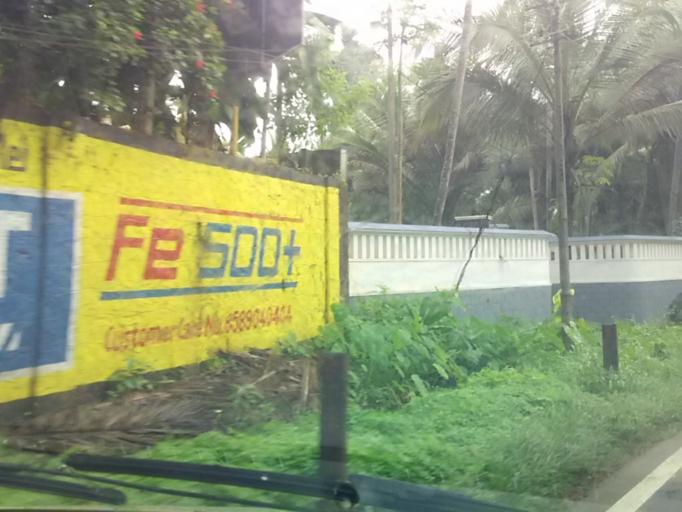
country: IN
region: Kerala
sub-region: Kozhikode
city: Kunnamangalam
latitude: 11.3111
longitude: 75.9141
